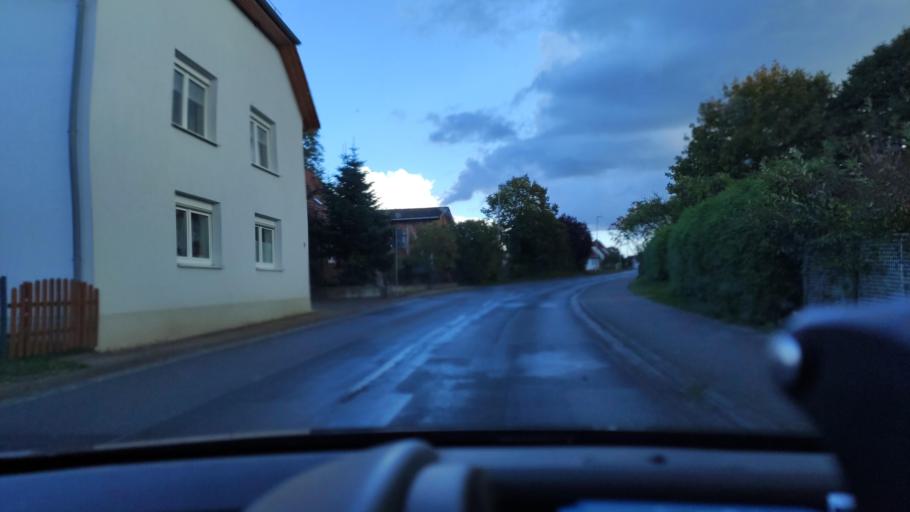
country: DE
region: Mecklenburg-Vorpommern
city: Tarnow
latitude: 53.7770
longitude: 12.0213
